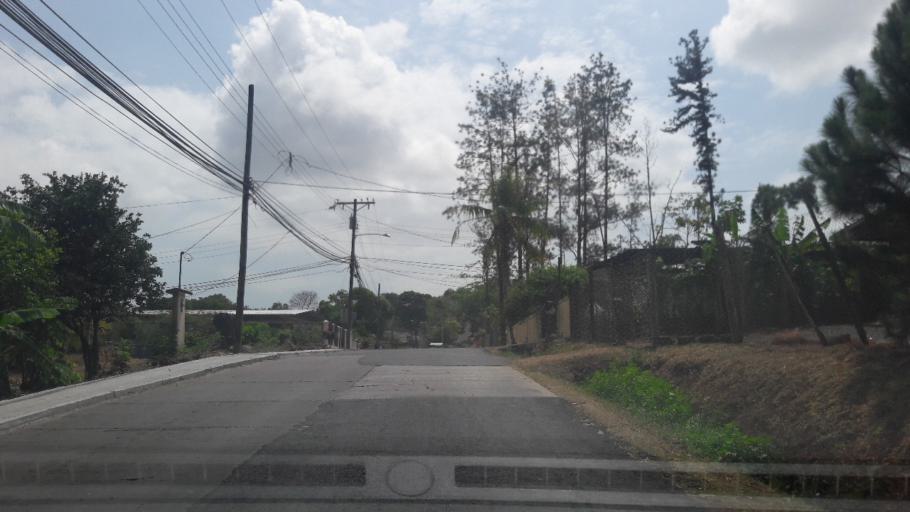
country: PA
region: Panama
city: Alcalde Diaz
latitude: 9.1373
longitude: -79.5527
